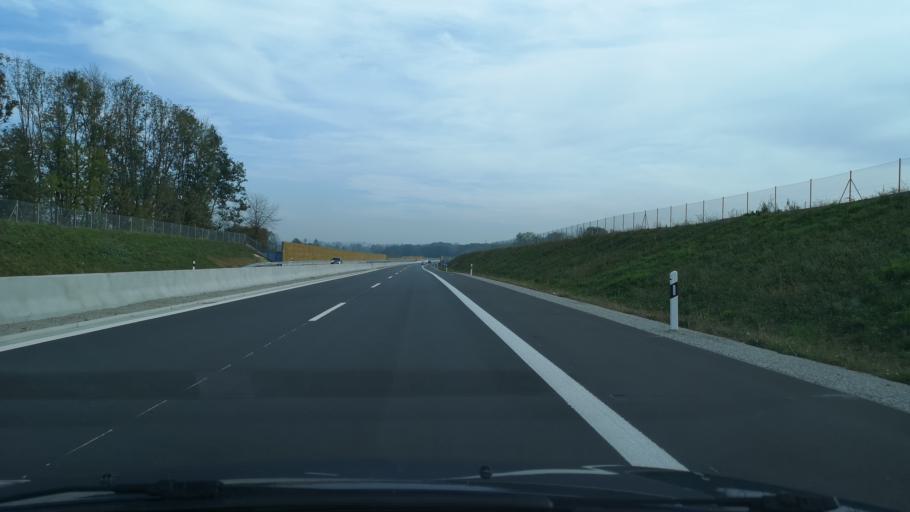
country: DE
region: Bavaria
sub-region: Upper Bavaria
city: Schwindegg
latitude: 48.2532
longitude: 12.2234
